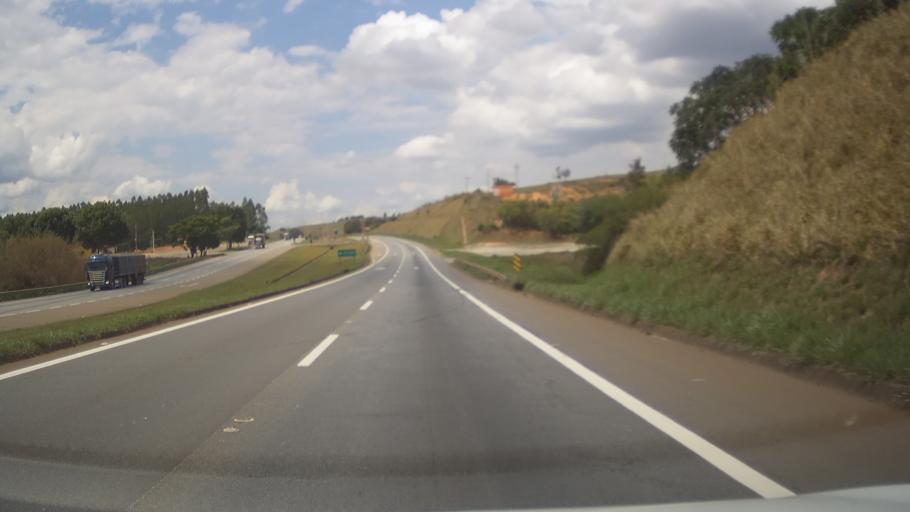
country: BR
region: Minas Gerais
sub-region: Nepomuceno
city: Nepomuceno
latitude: -21.3066
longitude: -45.1585
